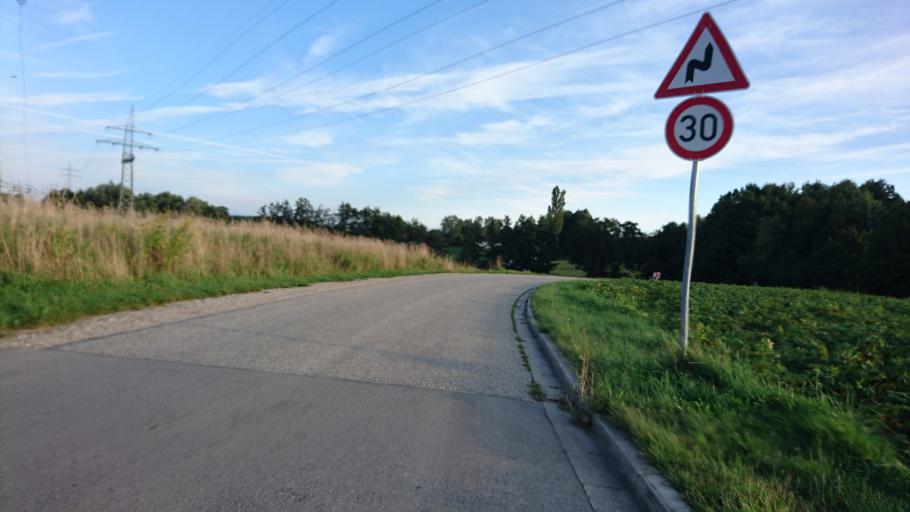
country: DE
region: Bavaria
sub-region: Upper Bavaria
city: Markt Schwaben
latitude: 48.1866
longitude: 11.8475
